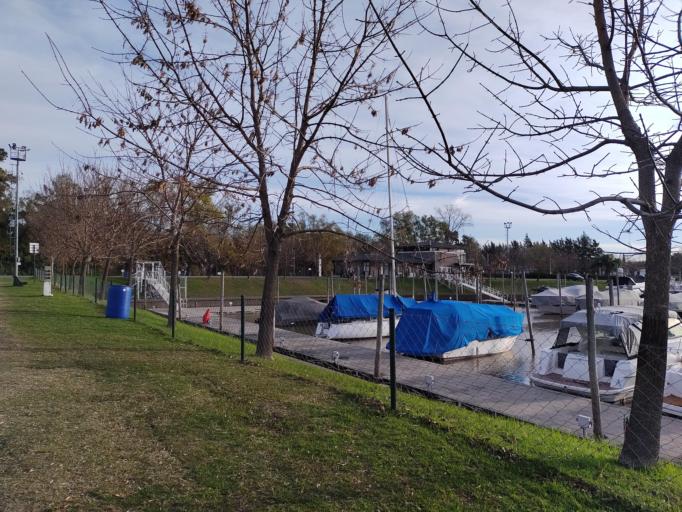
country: AR
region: Buenos Aires
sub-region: Partido de San Isidro
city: San Isidro
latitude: -34.4438
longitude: -58.5317
